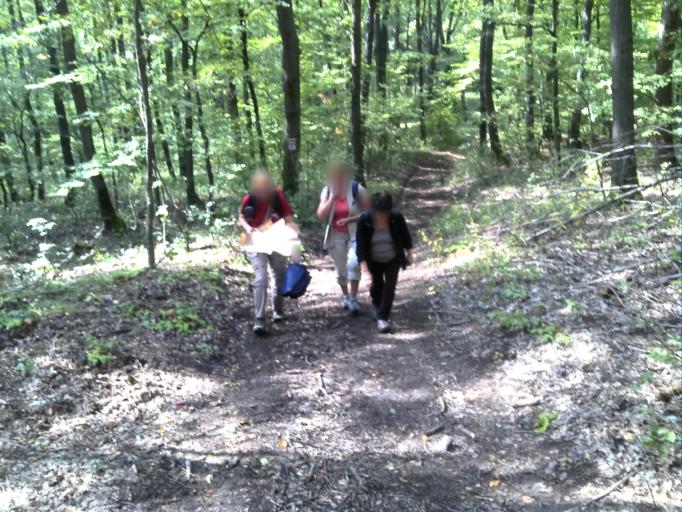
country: HU
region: Borsod-Abauj-Zemplen
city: Satoraljaujhely
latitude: 48.3926
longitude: 21.6132
